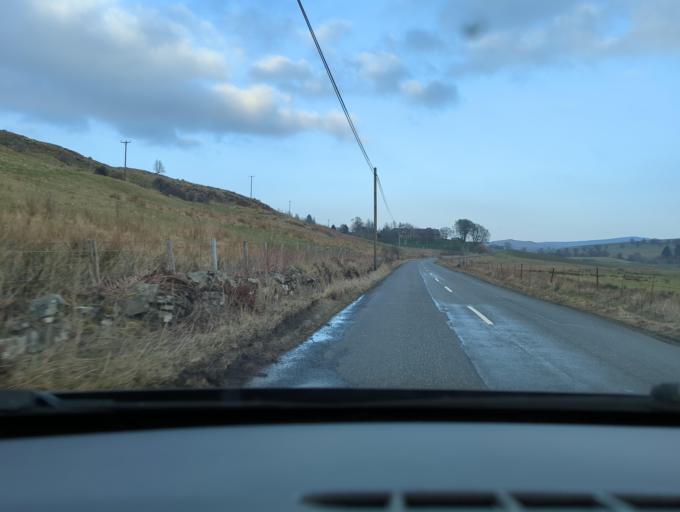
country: GB
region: Scotland
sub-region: Perth and Kinross
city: Aberfeldy
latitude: 56.5275
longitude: -3.7382
